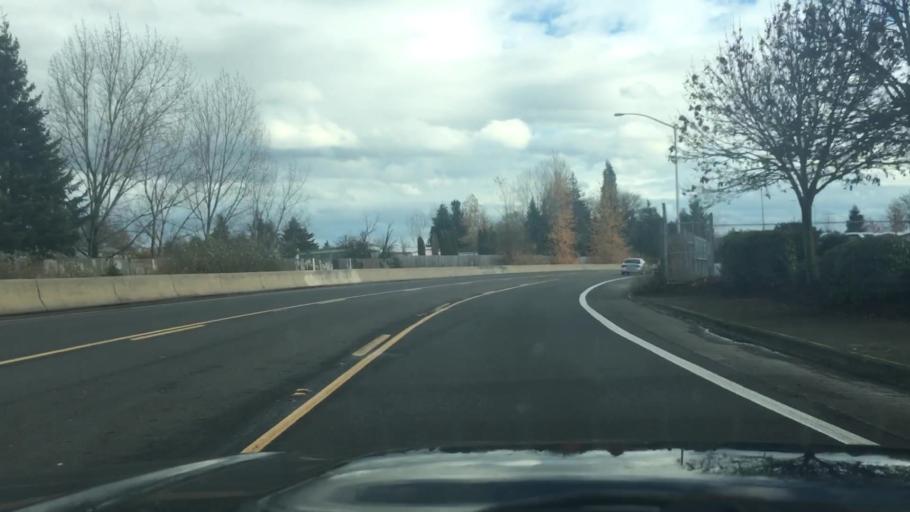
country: US
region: Oregon
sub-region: Lane County
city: Eugene
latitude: 44.0644
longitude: -123.1611
